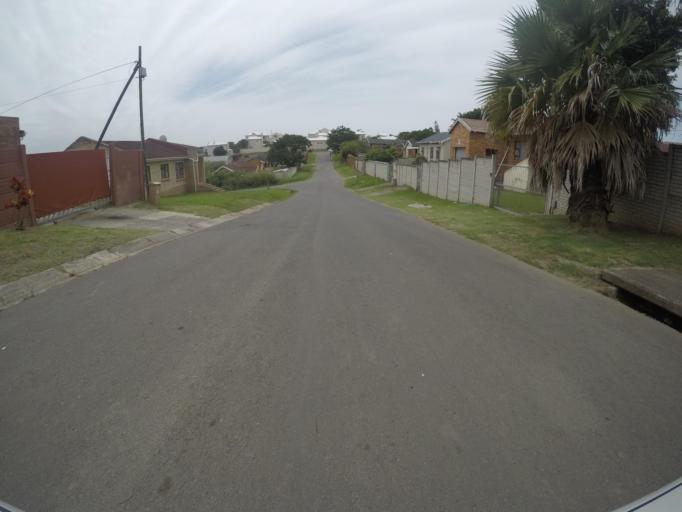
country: ZA
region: Eastern Cape
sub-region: Buffalo City Metropolitan Municipality
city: East London
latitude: -32.9608
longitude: 27.9312
